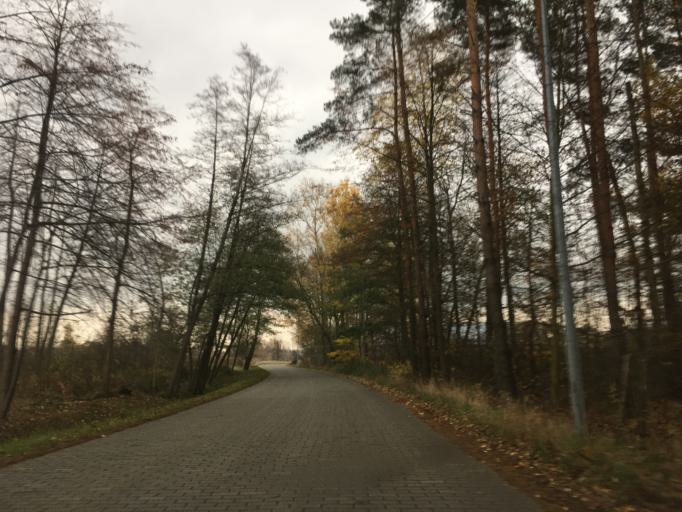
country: PL
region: Masovian Voivodeship
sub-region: Powiat piaseczynski
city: Lesznowola
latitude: 52.0424
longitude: 20.9375
